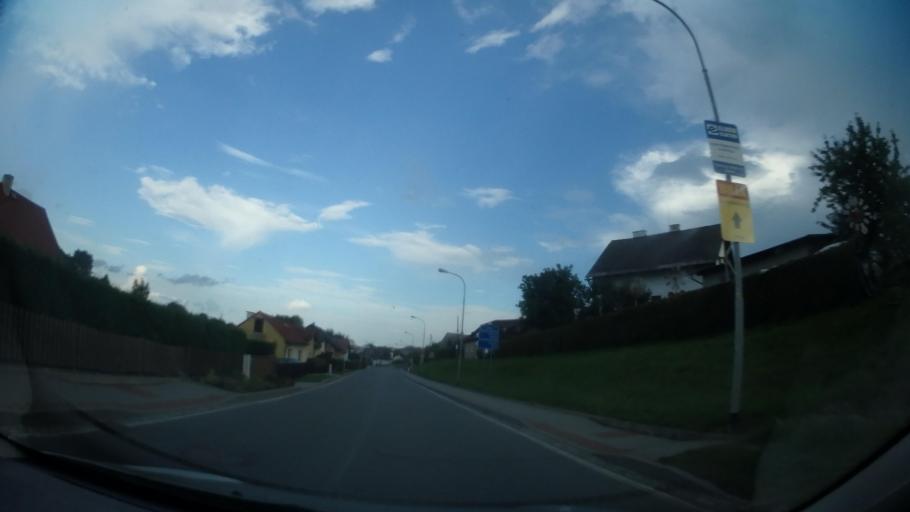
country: CZ
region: Olomoucky
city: Zabreh
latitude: 49.8852
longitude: 16.8584
